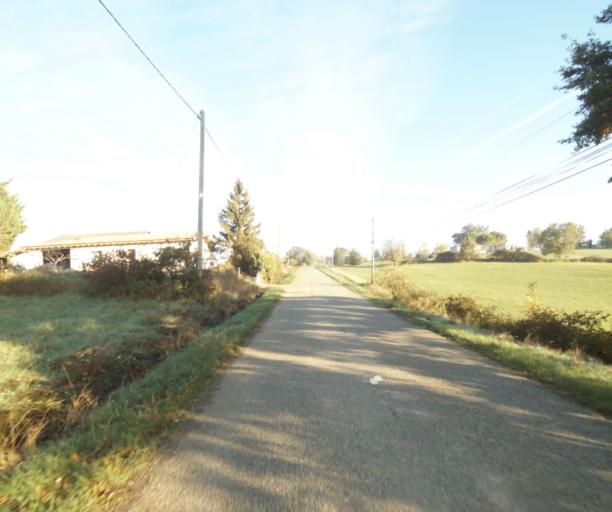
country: FR
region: Midi-Pyrenees
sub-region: Departement de la Haute-Garonne
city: Villemur-sur-Tarn
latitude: 43.9074
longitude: 1.4916
